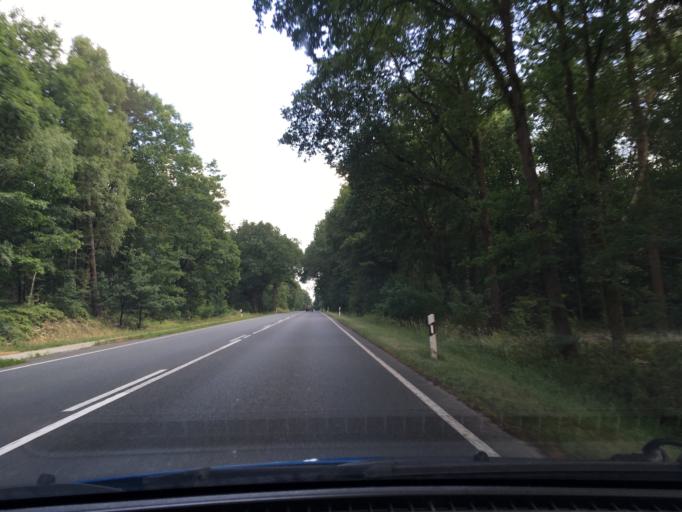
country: DE
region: Lower Saxony
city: Welle
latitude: 53.2765
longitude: 9.7981
